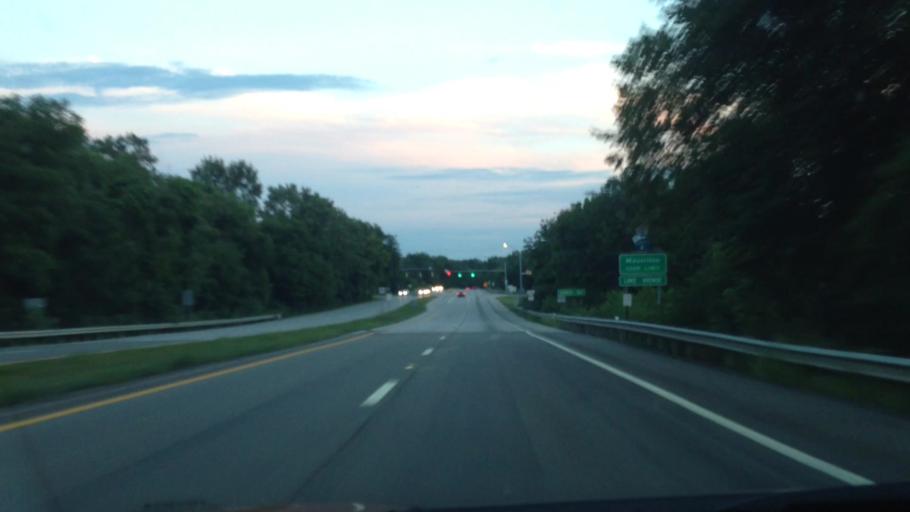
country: US
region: Ohio
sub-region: Stark County
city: Massillon
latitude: 40.8140
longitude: -81.5291
